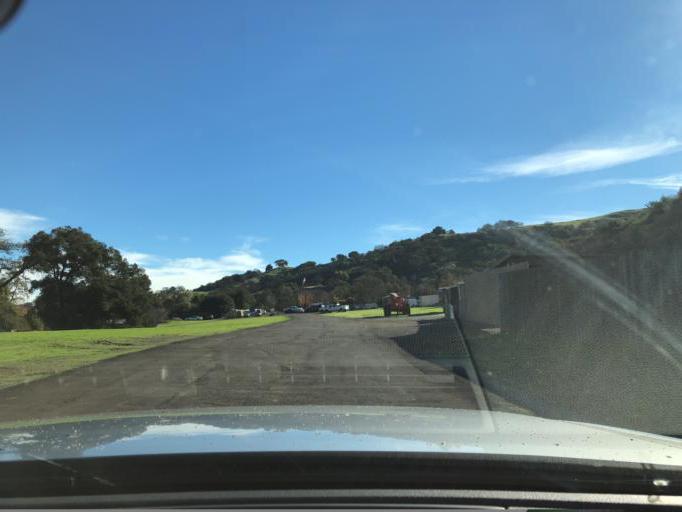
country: US
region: California
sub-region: Santa Clara County
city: Morgan Hill
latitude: 37.1550
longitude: -121.7107
